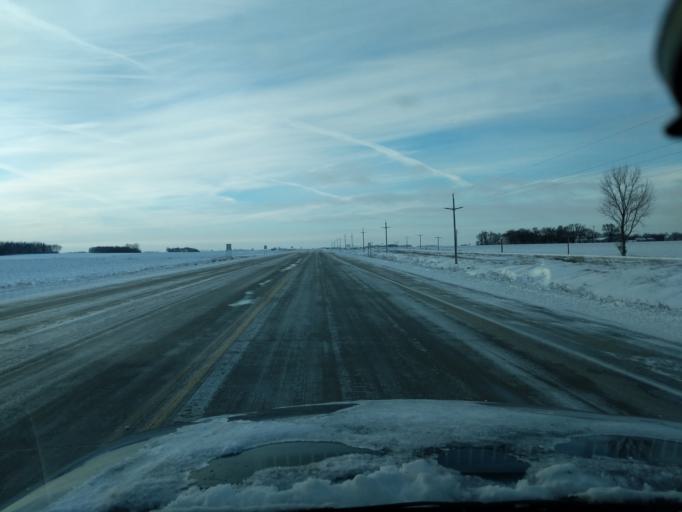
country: US
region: Minnesota
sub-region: Renville County
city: Hector
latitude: 44.7526
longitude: -94.7896
